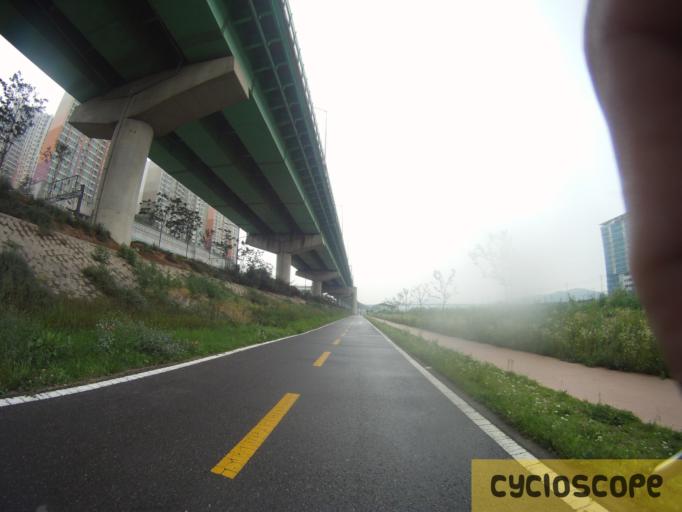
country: KR
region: Gyeonggi-do
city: Kwangmyong
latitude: 37.4476
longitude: 126.8971
